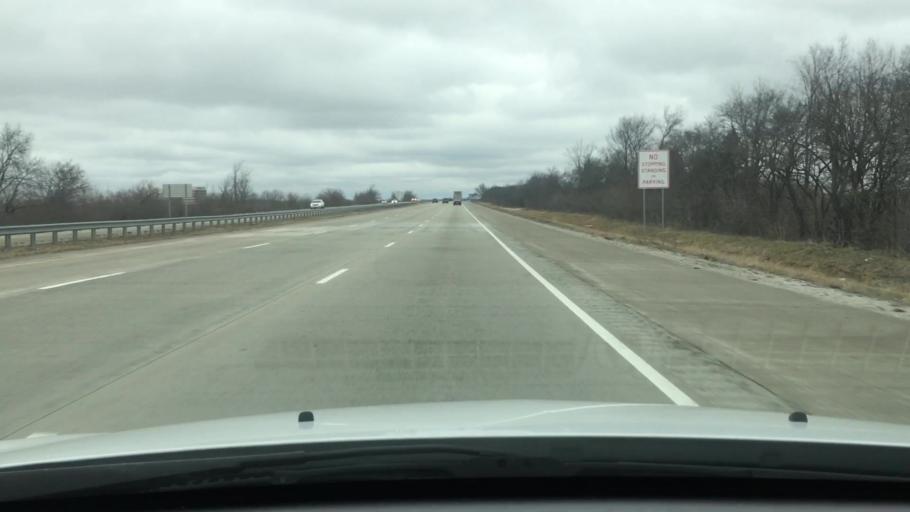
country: US
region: Indiana
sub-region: Tippecanoe County
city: Dayton
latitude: 40.3902
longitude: -86.7914
